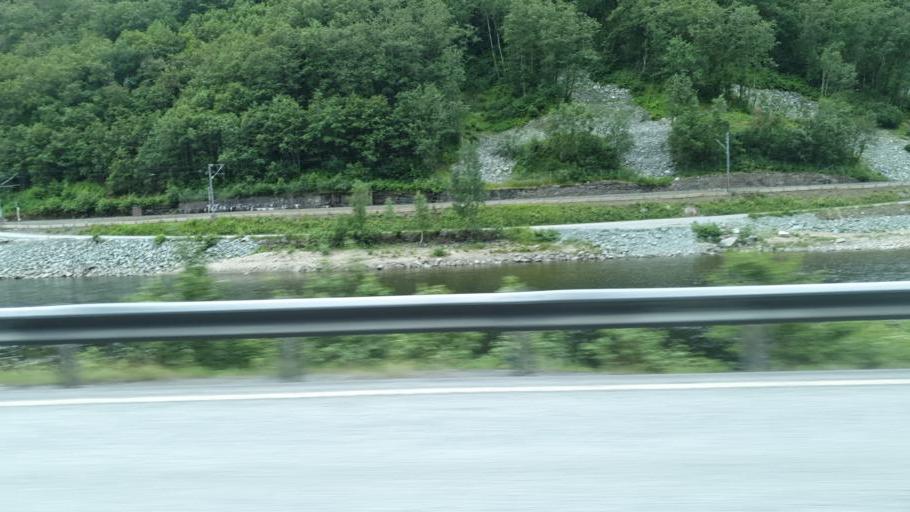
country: NO
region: Sor-Trondelag
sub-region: Midtre Gauldal
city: Storen
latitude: 63.0684
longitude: 10.2838
